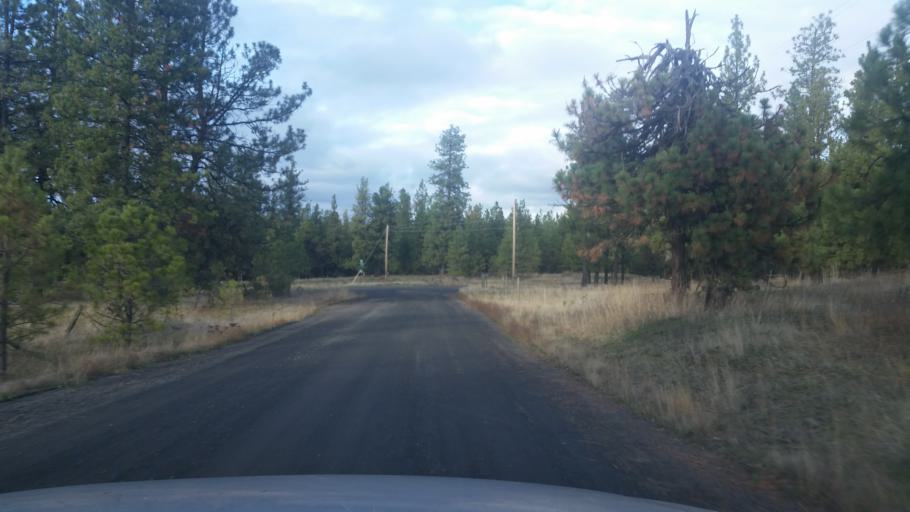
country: US
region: Washington
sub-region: Spokane County
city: Cheney
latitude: 47.4320
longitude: -117.4666
